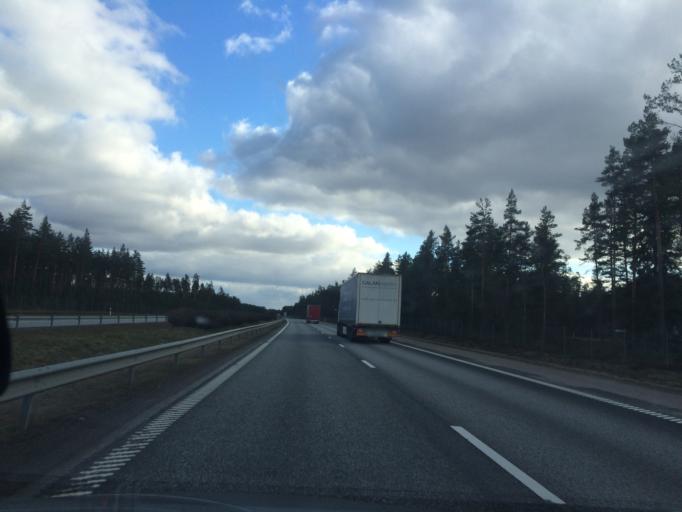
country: SE
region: Joenkoeping
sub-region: Vaggeryds Kommun
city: Skillingaryd
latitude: 57.3758
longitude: 14.1009
